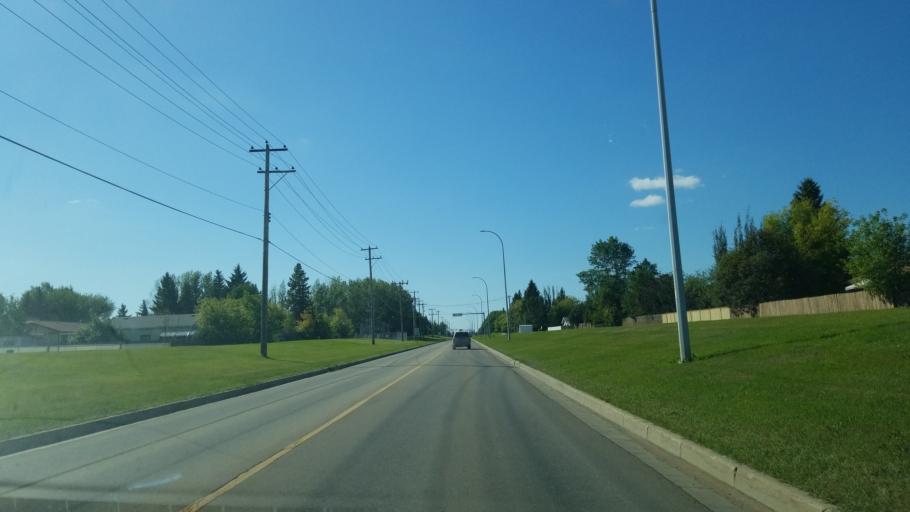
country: CA
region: Saskatchewan
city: Lloydminster
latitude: 53.2707
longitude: -110.0149
